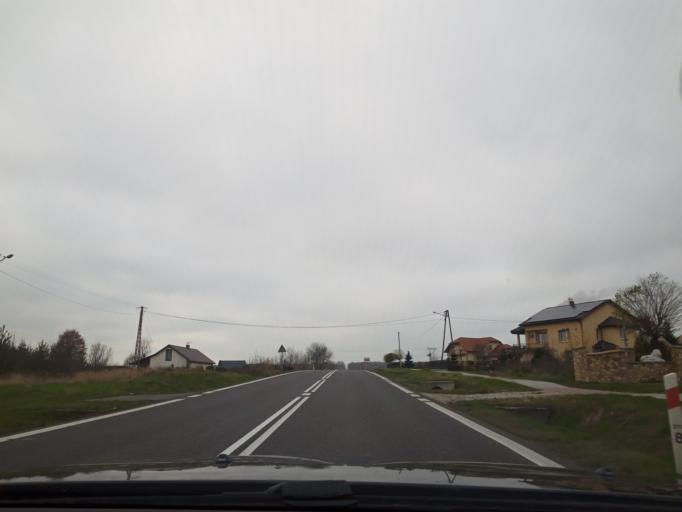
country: PL
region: Swietokrzyskie
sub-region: Powiat jedrzejowski
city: Imielno
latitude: 50.6067
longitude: 20.4882
